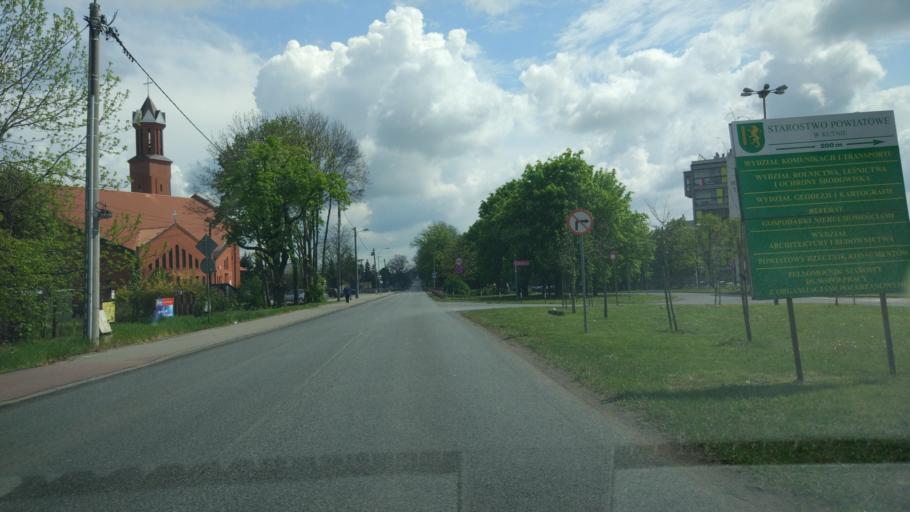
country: PL
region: Lodz Voivodeship
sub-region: Powiat kutnowski
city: Kutno
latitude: 52.2286
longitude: 19.3741
